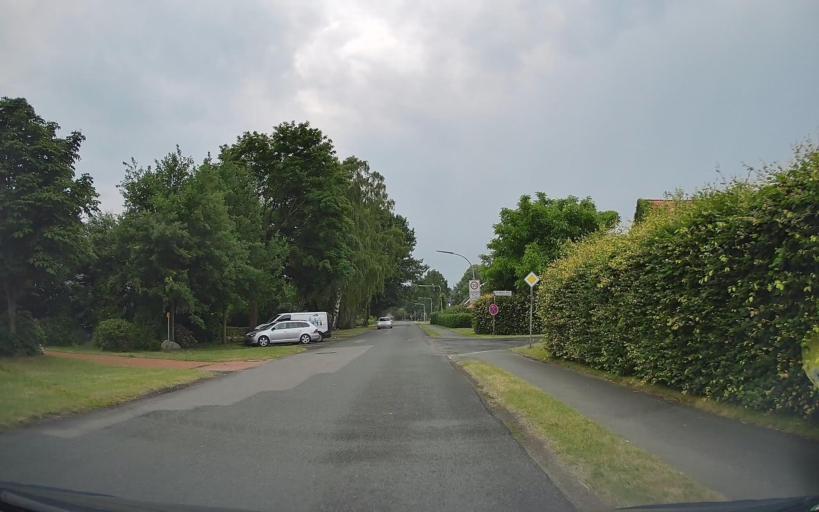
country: DE
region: Lower Saxony
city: Friesoythe
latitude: 53.0154
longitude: 7.8595
